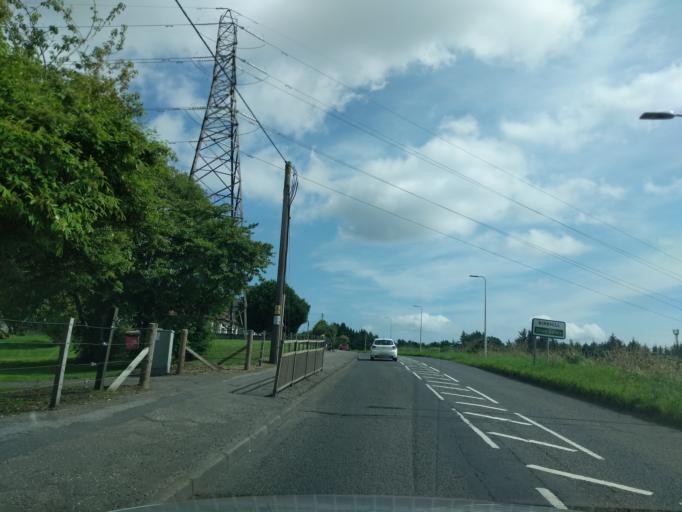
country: GB
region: Scotland
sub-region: Angus
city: Muirhead
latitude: 56.4958
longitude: -3.0637
